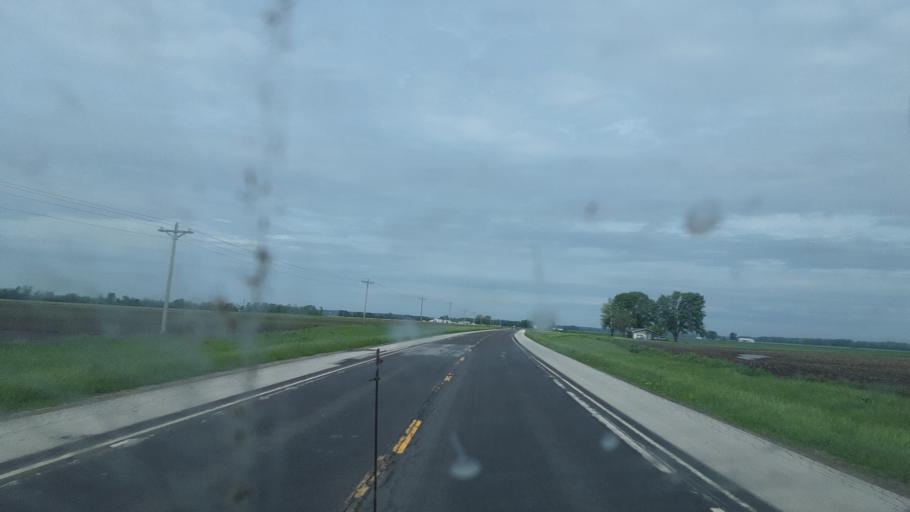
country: US
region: Illinois
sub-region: Hancock County
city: Warsaw
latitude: 40.3763
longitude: -91.4901
